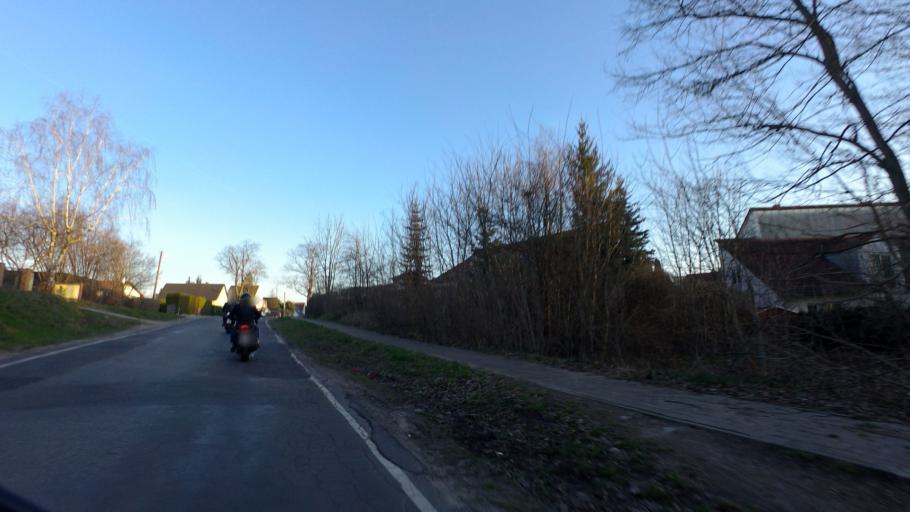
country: DE
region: Berlin
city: Hellersdorf
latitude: 52.5575
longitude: 13.6328
